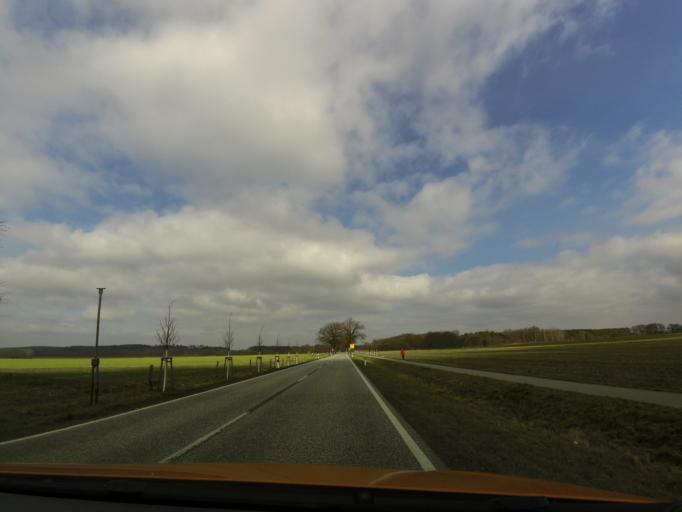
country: DE
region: Brandenburg
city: Rathenow
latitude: 52.6778
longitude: 12.3522
